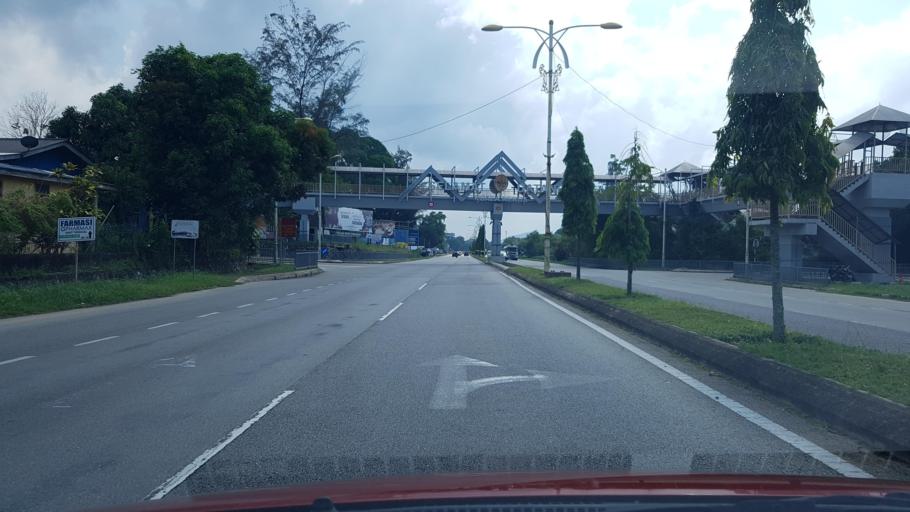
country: MY
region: Terengganu
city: Kuala Terengganu
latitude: 5.3392
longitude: 103.1063
